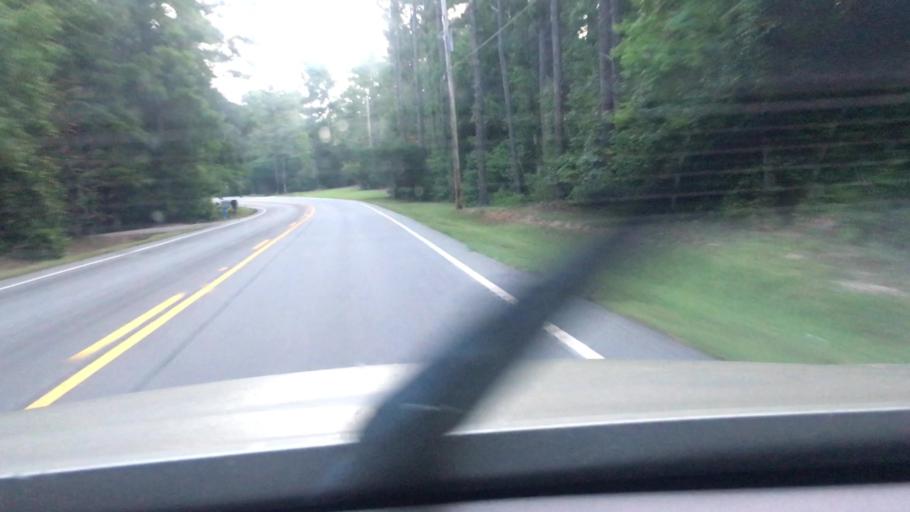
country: US
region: South Carolina
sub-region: Lexington County
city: Irmo
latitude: 34.1396
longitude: -81.1893
